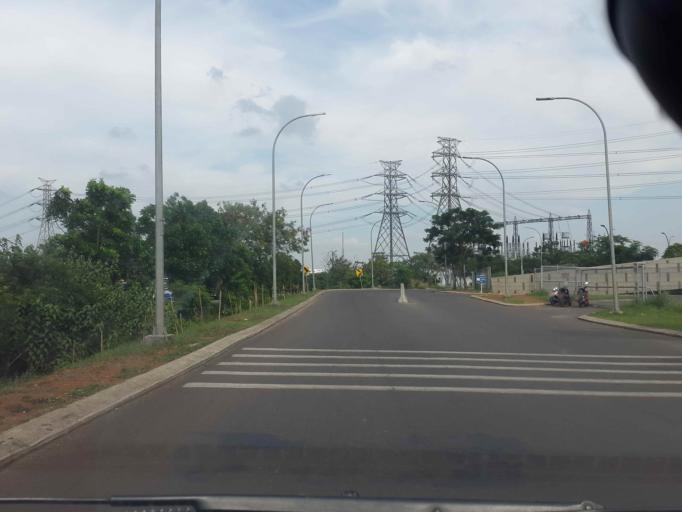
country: ID
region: West Java
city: Ciputat
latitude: -6.2201
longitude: 106.6542
